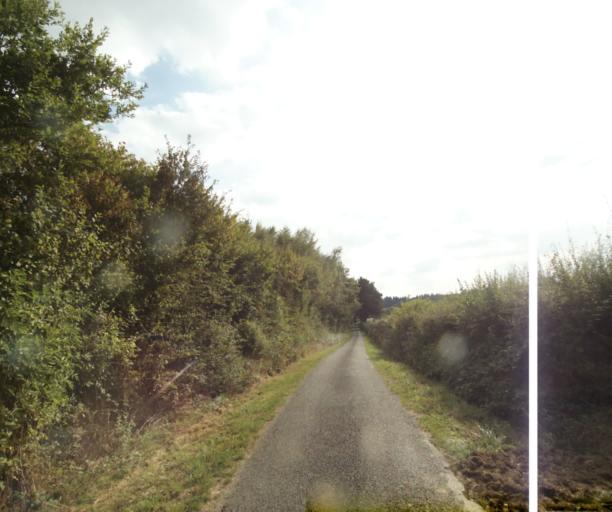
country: FR
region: Bourgogne
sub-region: Departement de Saone-et-Loire
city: Palinges
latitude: 46.5160
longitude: 4.2459
